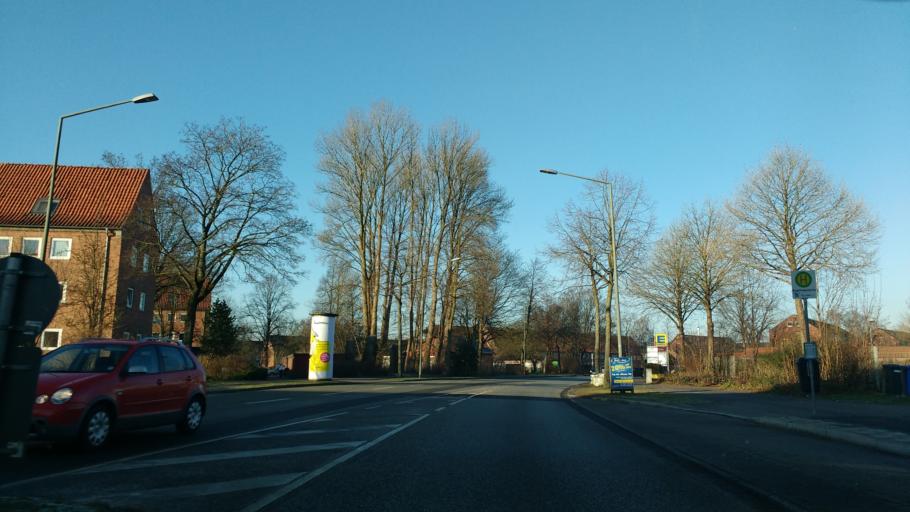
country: DE
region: Schleswig-Holstein
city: Neumunster
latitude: 54.0772
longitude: 9.9627
